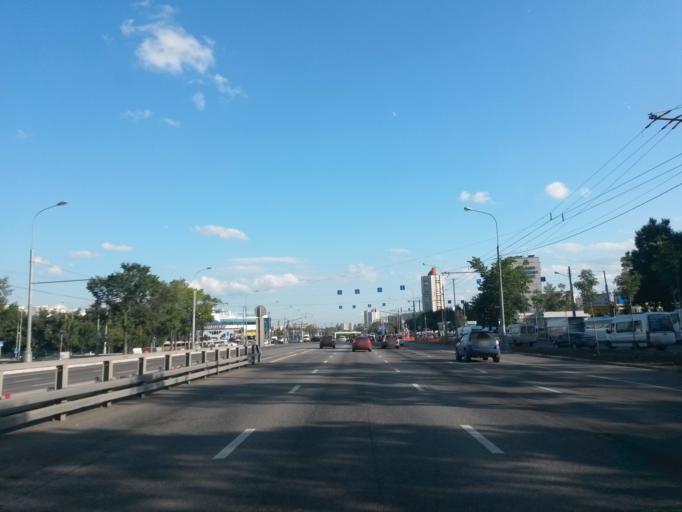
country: RU
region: Moscow
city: Orekhovo-Borisovo
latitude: 55.6125
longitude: 37.7165
